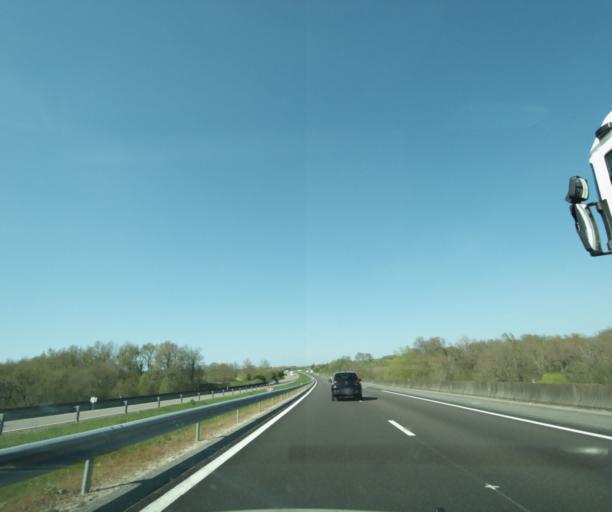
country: FR
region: Bourgogne
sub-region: Departement de la Nievre
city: Cosne-Cours-sur-Loire
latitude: 47.4775
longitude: 2.9447
